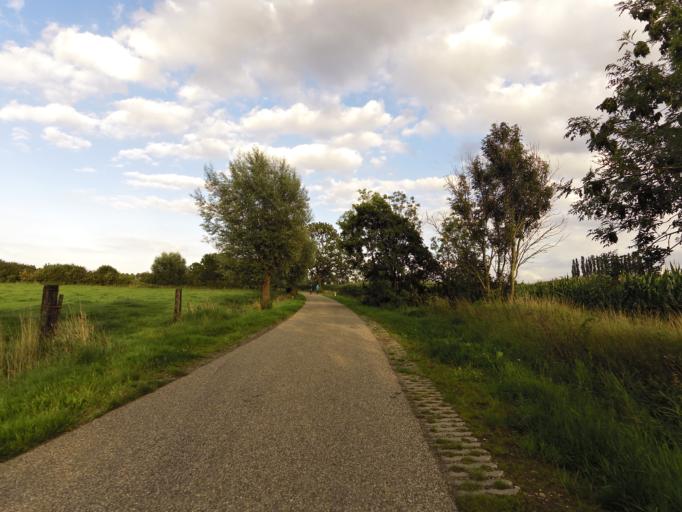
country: NL
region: Gelderland
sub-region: Gemeente Doesburg
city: Doesburg
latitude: 51.9767
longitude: 6.2064
